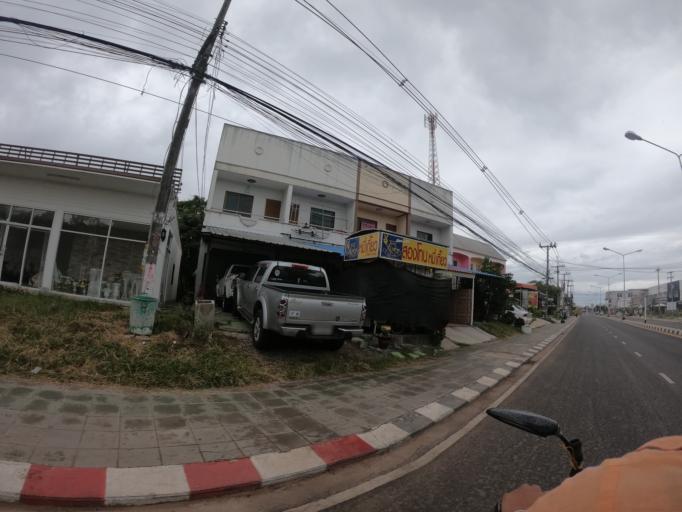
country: TH
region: Roi Et
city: Chiang Khwan
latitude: 16.1496
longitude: 103.8665
